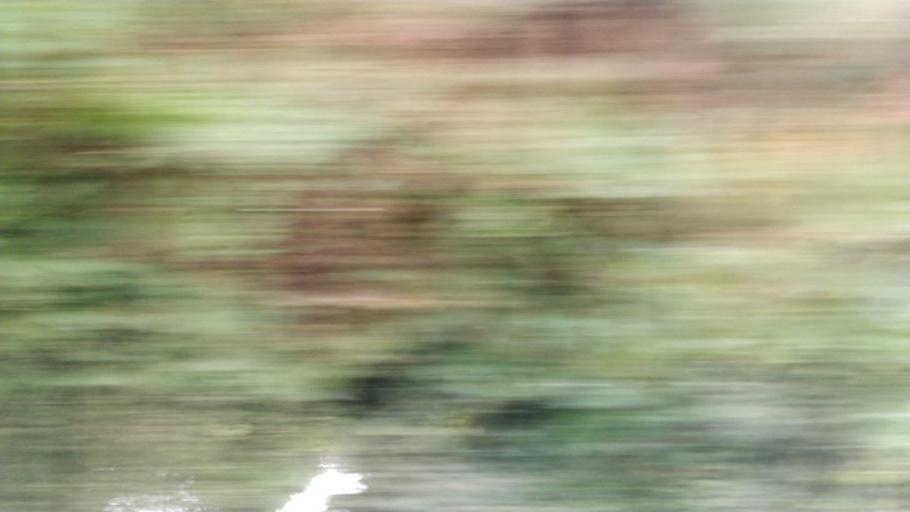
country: GB
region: England
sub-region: Lancashire
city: Parbold
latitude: 53.5892
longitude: -2.7637
